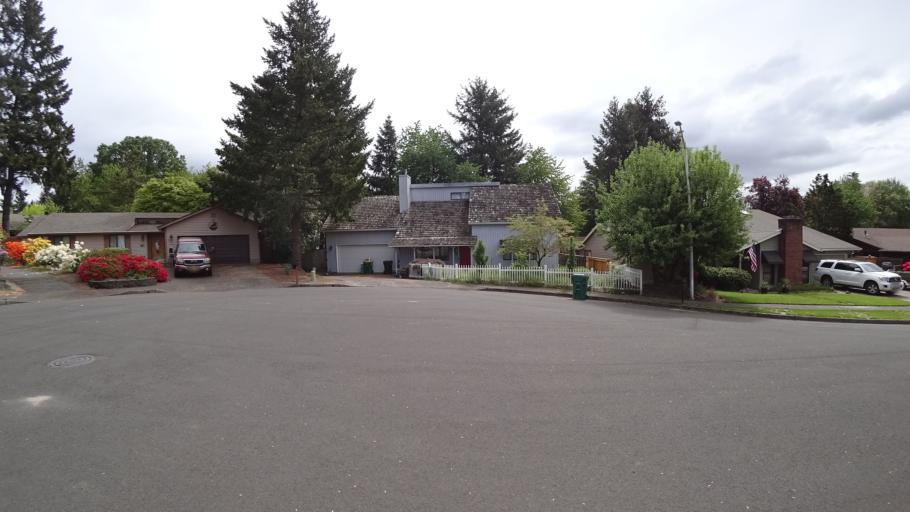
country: US
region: Oregon
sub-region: Washington County
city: Beaverton
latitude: 45.4712
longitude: -122.8138
